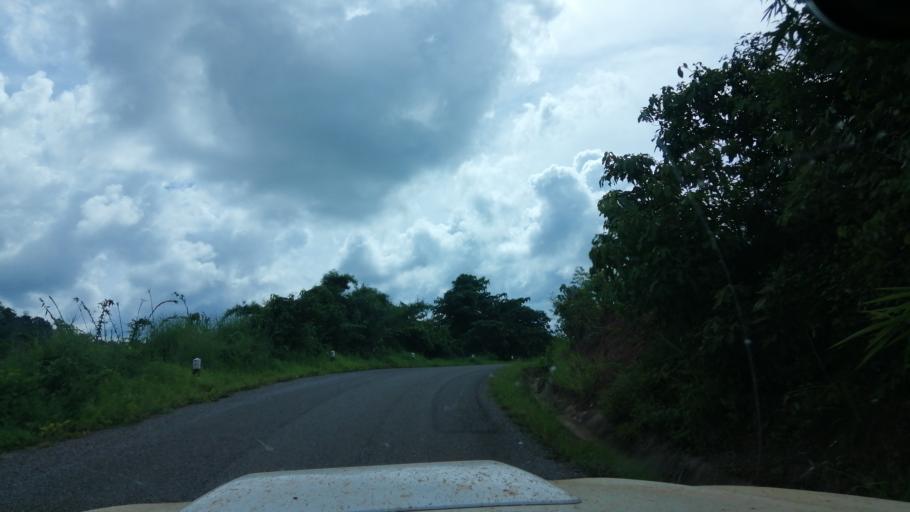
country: TH
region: Nan
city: Mae Charim
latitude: 18.3795
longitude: 101.1538
